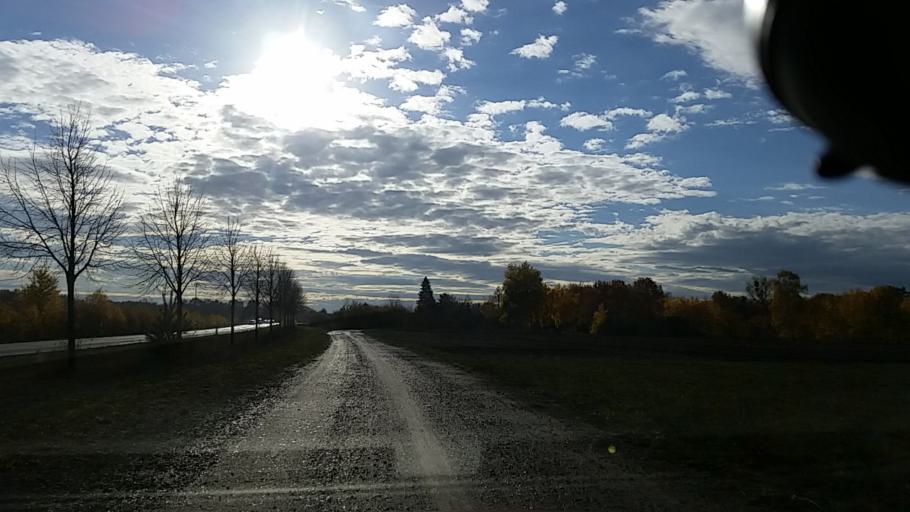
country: DE
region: Lower Saxony
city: Ruhen
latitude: 52.4583
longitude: 10.8346
